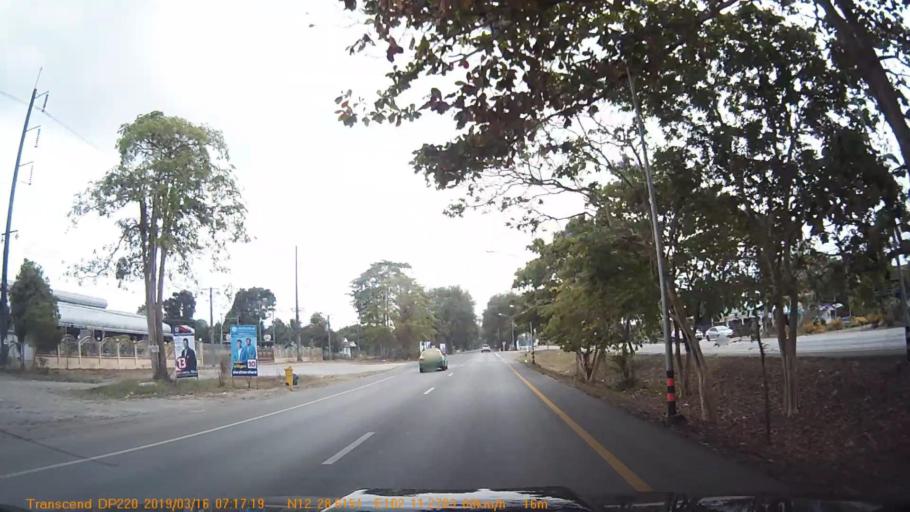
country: TH
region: Chanthaburi
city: Khlung
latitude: 12.4686
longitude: 102.1981
